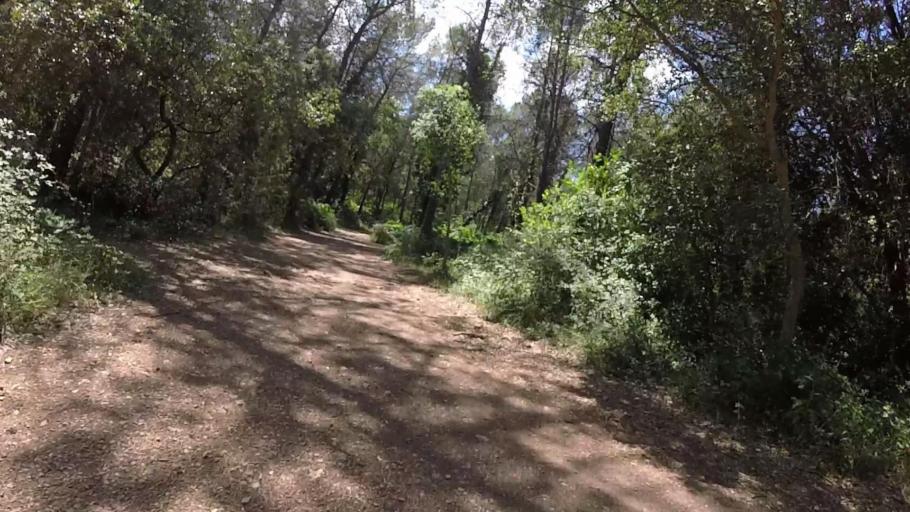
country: FR
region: Provence-Alpes-Cote d'Azur
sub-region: Departement des Alpes-Maritimes
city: Le Cannet
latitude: 43.5976
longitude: 7.0322
